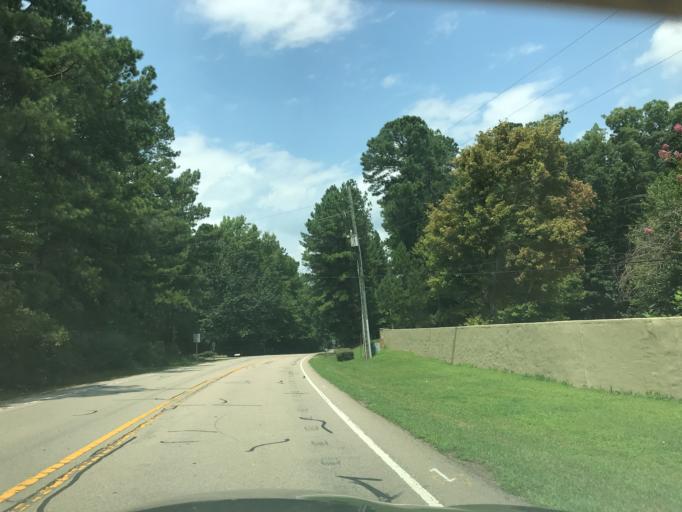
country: US
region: North Carolina
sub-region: Wake County
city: West Raleigh
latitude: 35.8290
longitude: -78.7147
